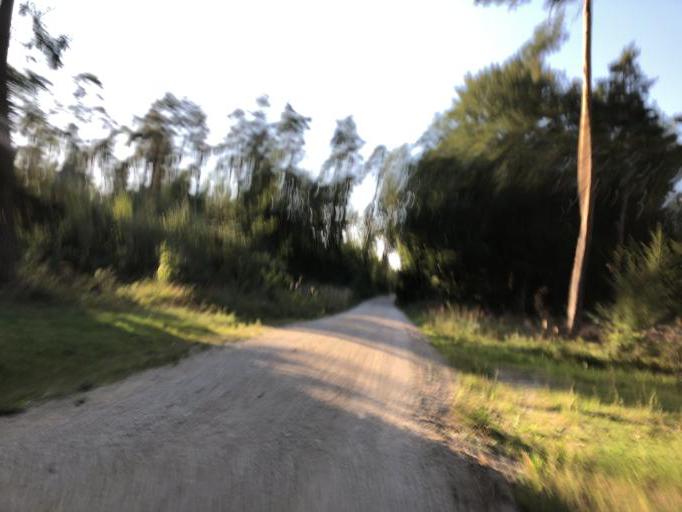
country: DE
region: Bavaria
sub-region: Regierungsbezirk Mittelfranken
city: Uttenreuth
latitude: 49.5728
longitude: 11.0816
